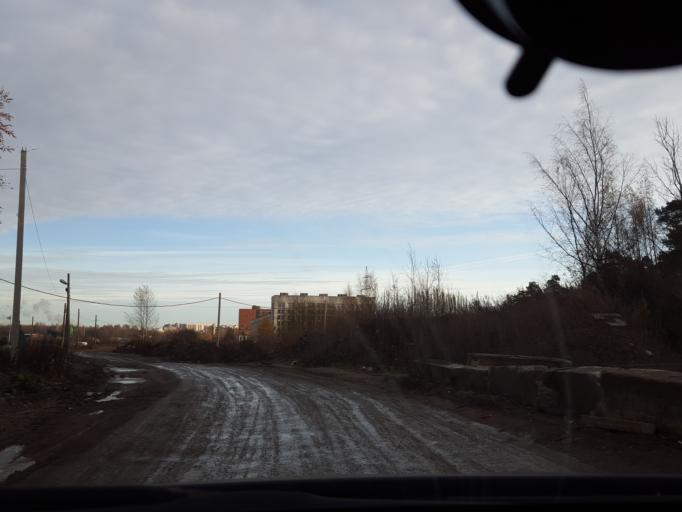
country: RU
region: St.-Petersburg
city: Kolomyagi
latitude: 60.0374
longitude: 30.2708
